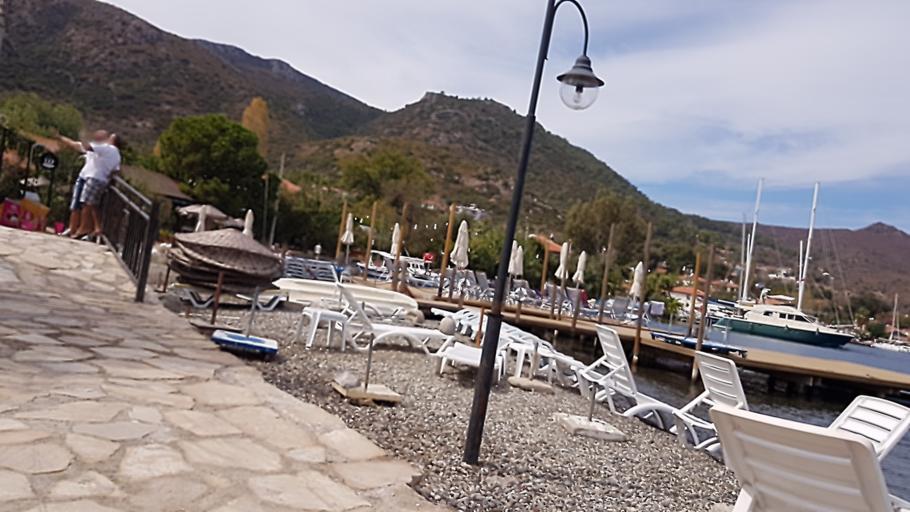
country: TR
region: Mugla
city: Bozburun
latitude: 36.7071
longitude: 28.0916
